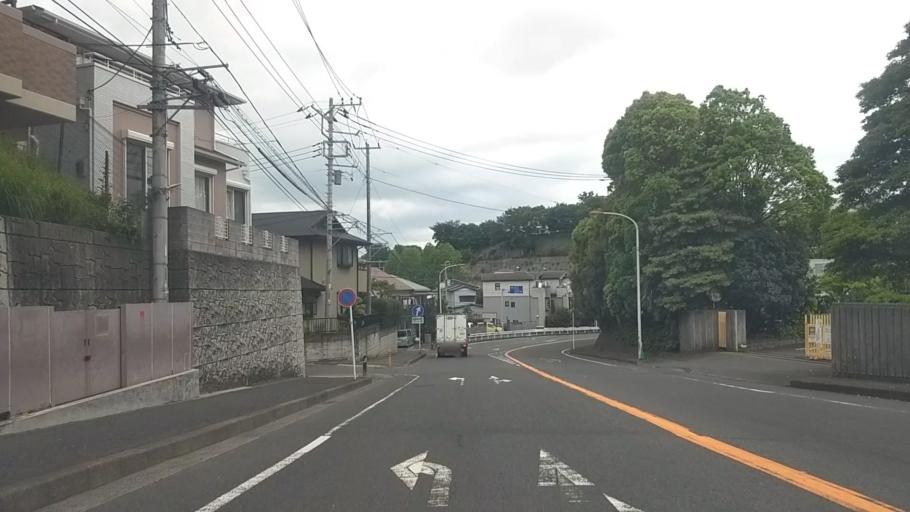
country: JP
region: Kanagawa
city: Fujisawa
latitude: 35.3505
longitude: 139.4689
